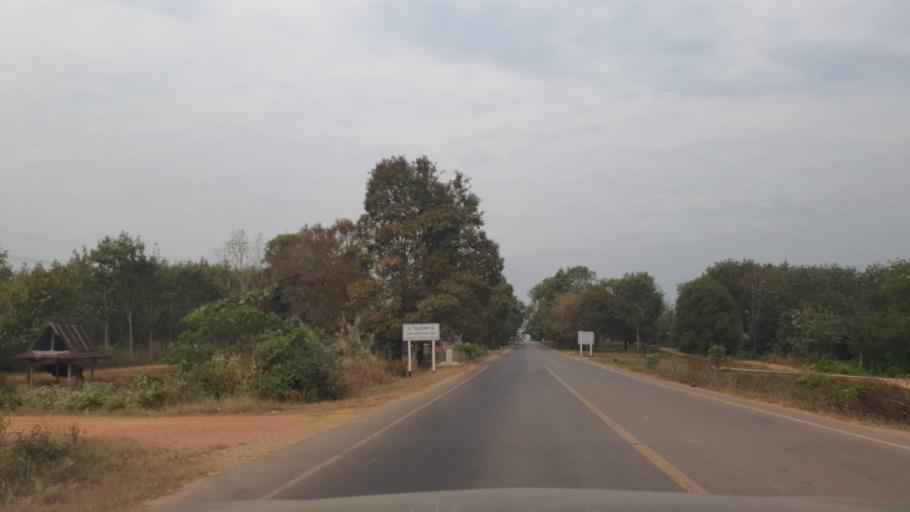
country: TH
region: Changwat Bueng Kan
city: Bung Khla
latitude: 18.2415
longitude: 104.0220
